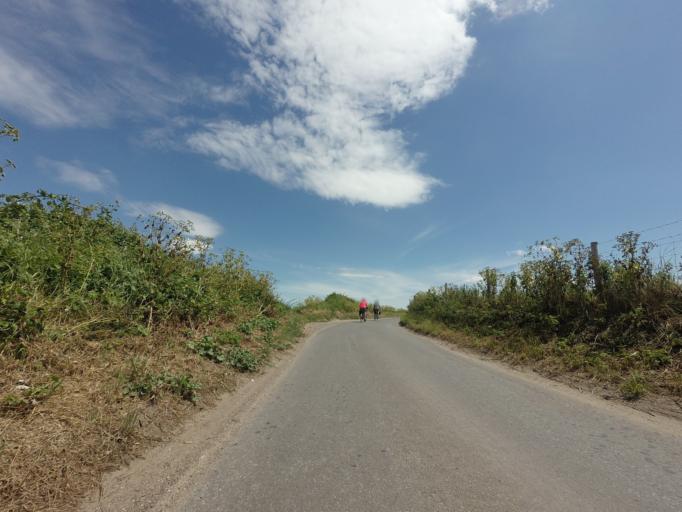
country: GB
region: England
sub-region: Kent
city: Cliffe
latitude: 51.4620
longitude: 0.5059
